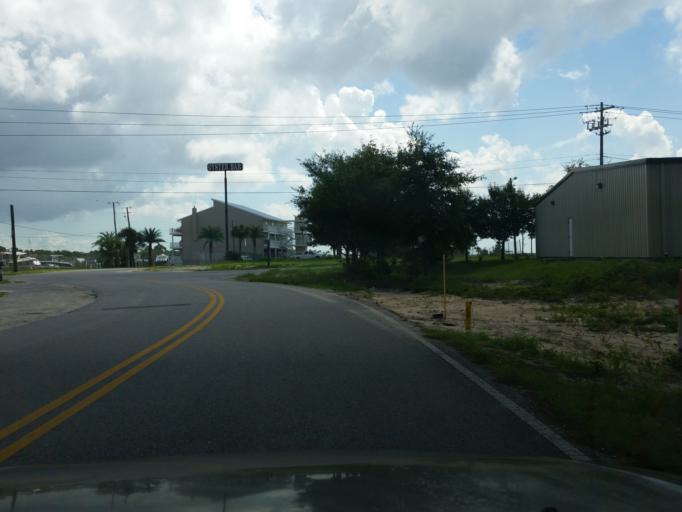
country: US
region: Alabama
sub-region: Baldwin County
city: Orange Beach
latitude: 30.3108
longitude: -87.4271
